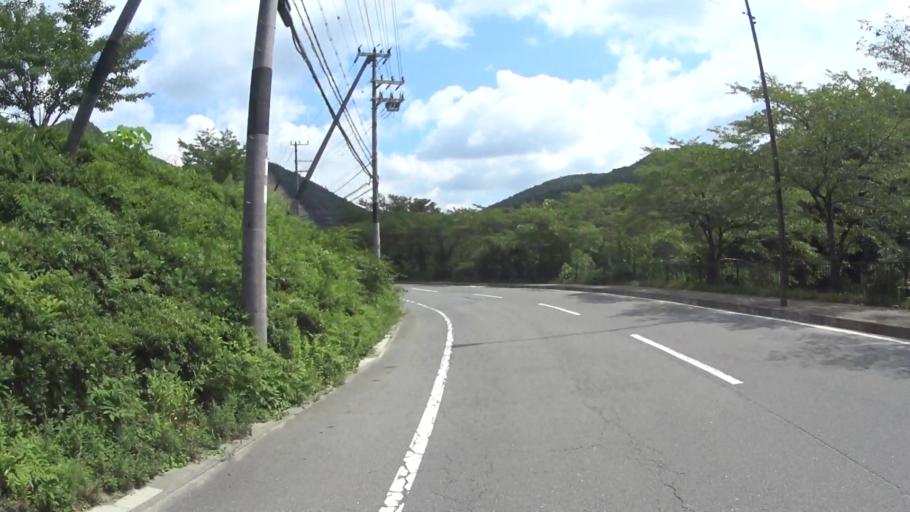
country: JP
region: Kyoto
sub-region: Kyoto-shi
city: Kamigyo-ku
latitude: 35.0947
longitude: 135.7677
